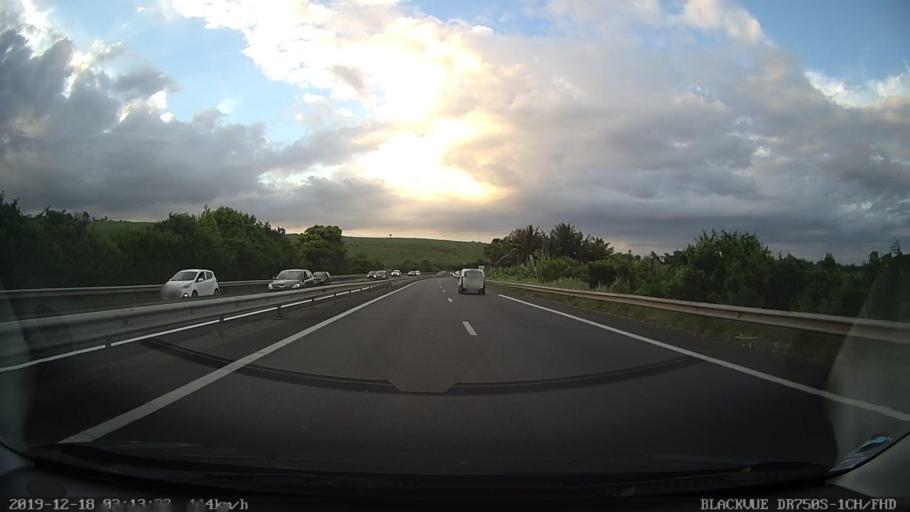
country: RE
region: Reunion
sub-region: Reunion
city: Sainte-Suzanne
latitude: -20.9268
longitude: 55.6287
